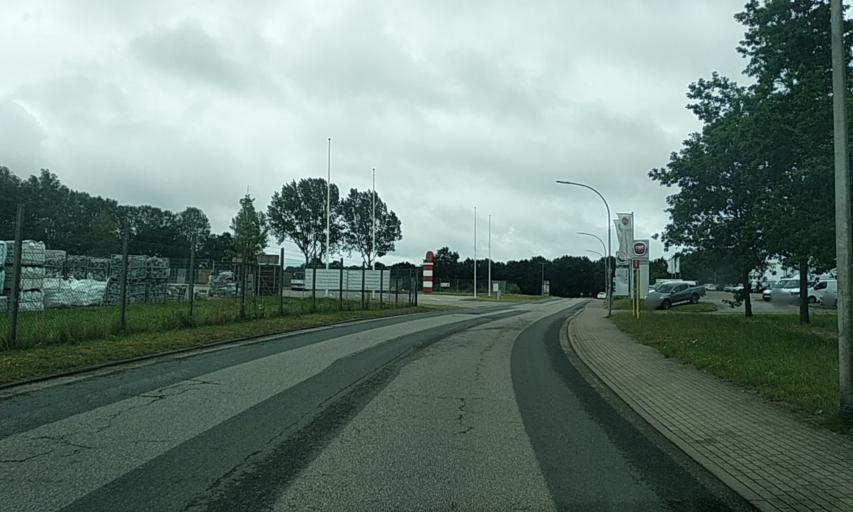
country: DE
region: Schleswig-Holstein
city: Schleswig
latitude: 54.5319
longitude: 9.5838
